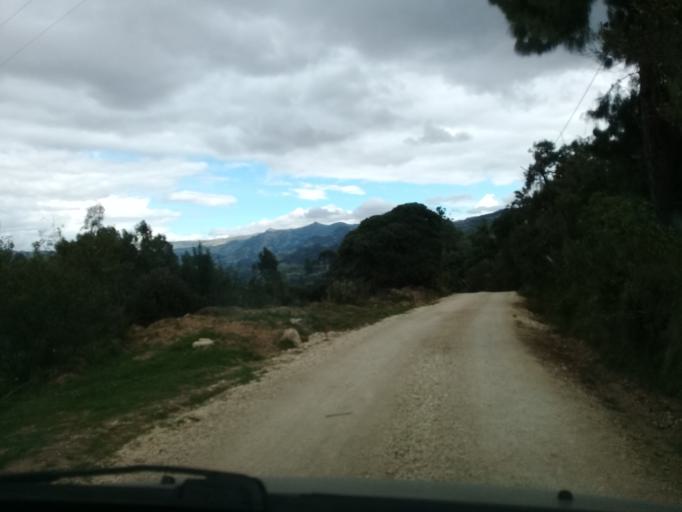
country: CO
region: Cundinamarca
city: Lenguazaque
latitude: 5.2878
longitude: -73.7295
